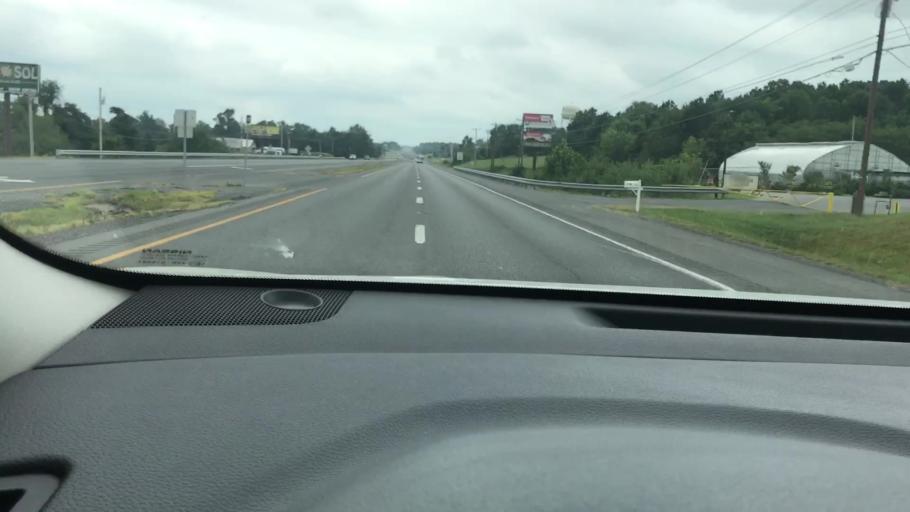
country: US
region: Kentucky
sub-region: Calloway County
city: Murray
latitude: 36.6680
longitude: -88.3040
